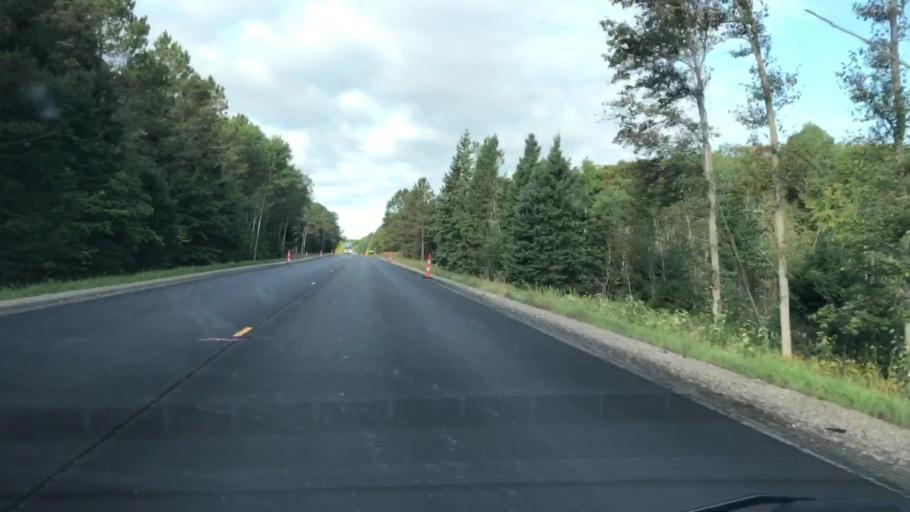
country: US
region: Michigan
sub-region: Luce County
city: Newberry
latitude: 46.3464
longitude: -85.0155
